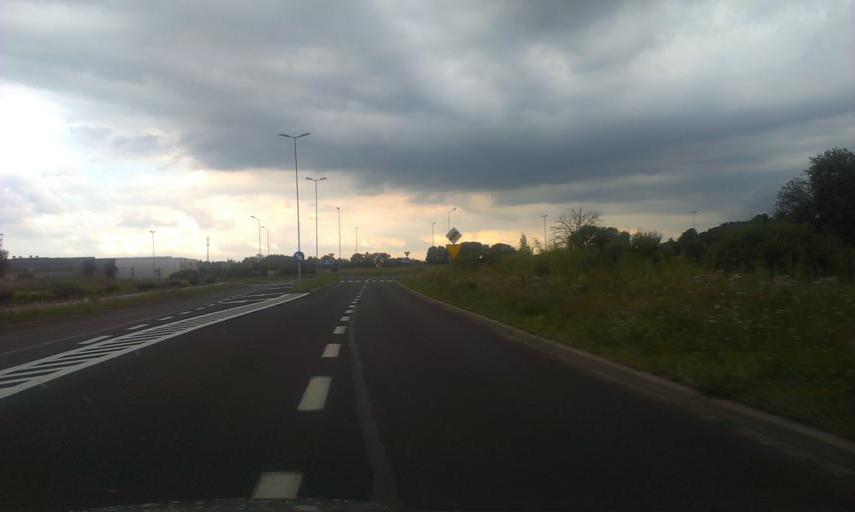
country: PL
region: West Pomeranian Voivodeship
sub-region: Koszalin
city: Koszalin
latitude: 54.1875
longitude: 16.1440
